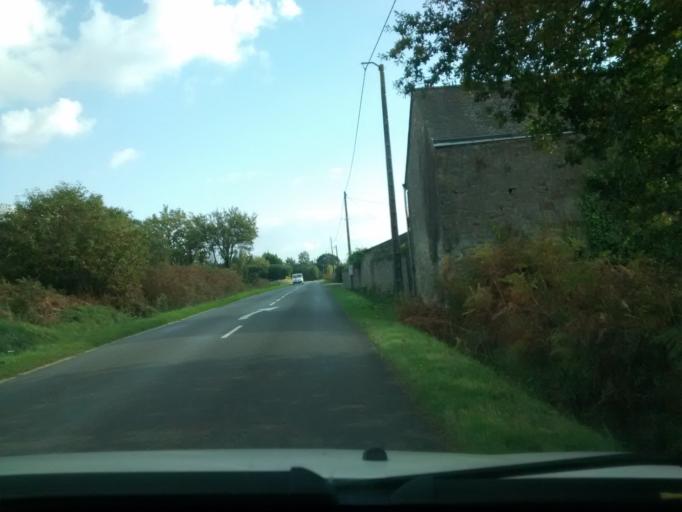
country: FR
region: Pays de la Loire
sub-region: Departement de la Loire-Atlantique
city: Sautron
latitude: 47.2883
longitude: -1.6559
